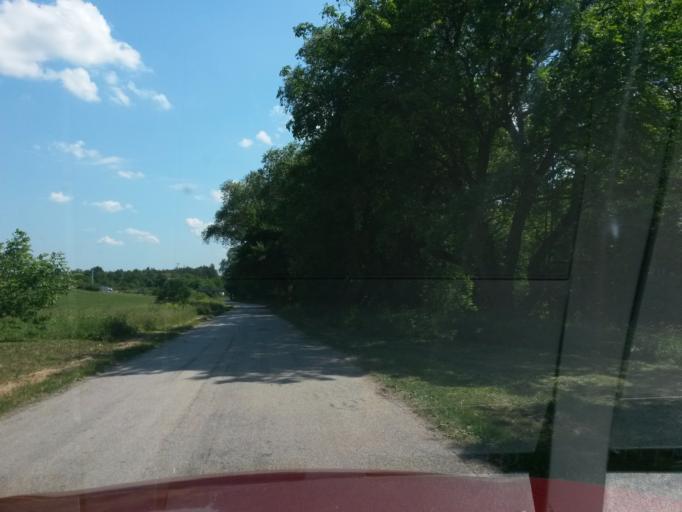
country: SK
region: Kosicky
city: Medzev
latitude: 48.6084
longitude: 20.8364
